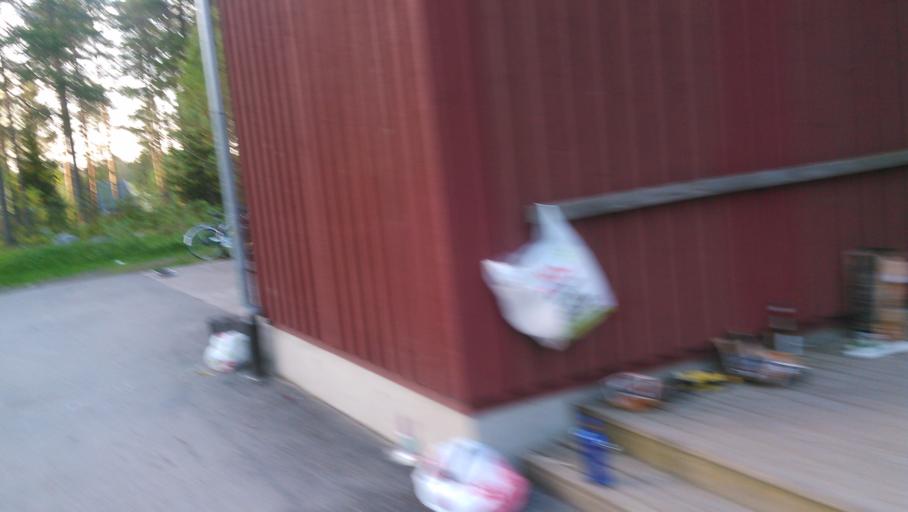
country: SE
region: Vaesterbotten
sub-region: Umea Kommun
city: Umea
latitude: 63.8168
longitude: 20.3114
